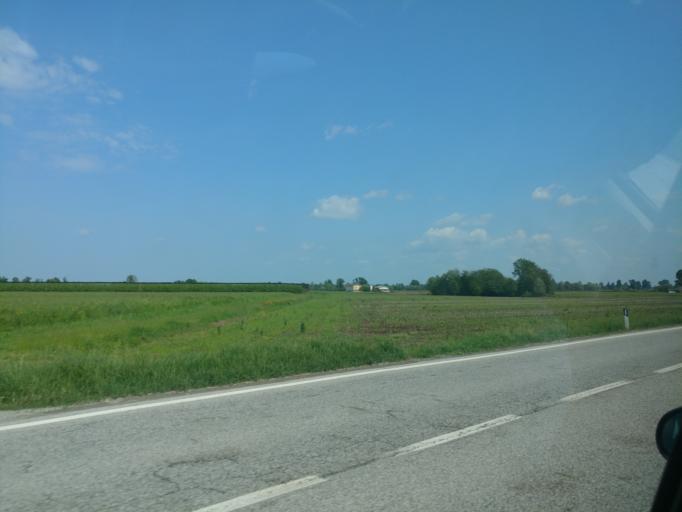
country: IT
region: Piedmont
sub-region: Provincia di Cuneo
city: Carde
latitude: 44.7321
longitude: 7.4249
